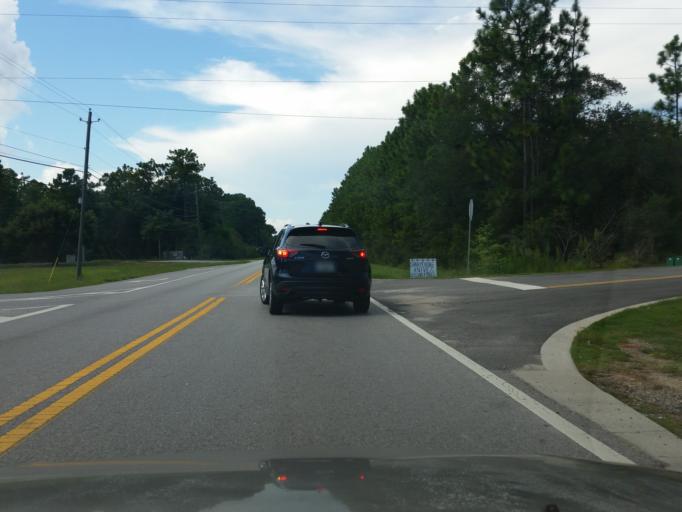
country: US
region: Florida
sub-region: Escambia County
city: Myrtle Grove
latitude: 30.3970
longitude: -87.4006
